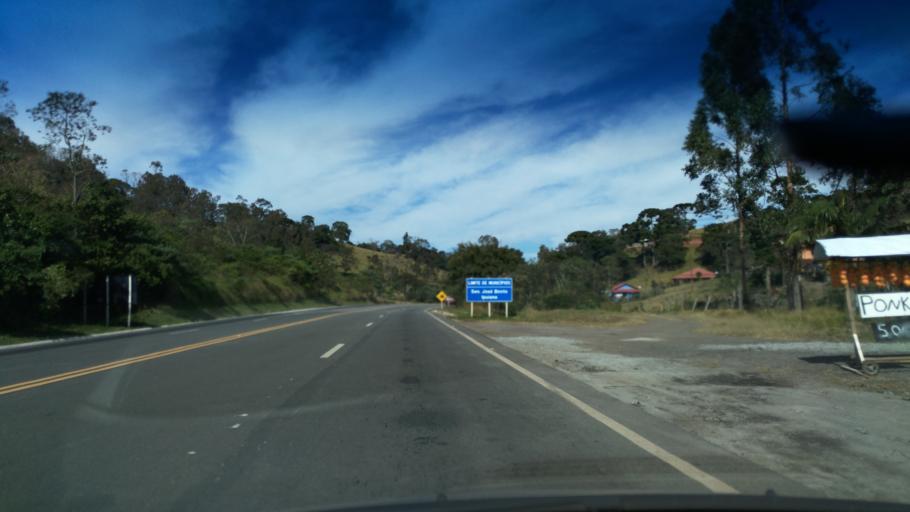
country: BR
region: Minas Gerais
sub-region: Borda Da Mata
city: Borda da Mata
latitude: -22.1255
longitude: -46.1814
